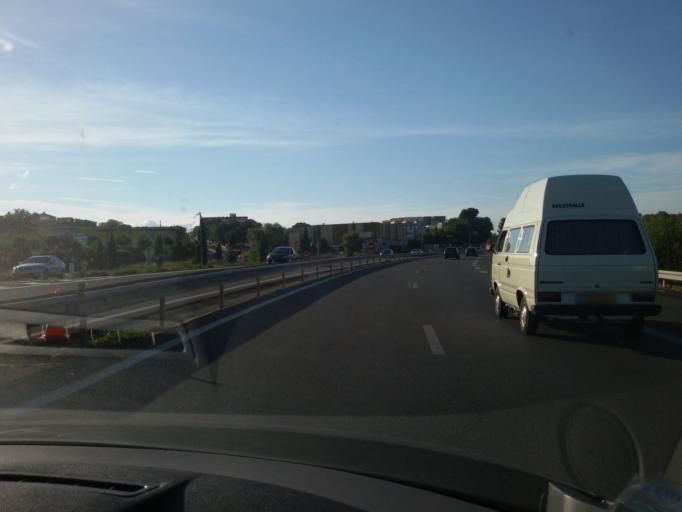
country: FR
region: Languedoc-Roussillon
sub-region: Departement de l'Herault
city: Juvignac
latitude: 43.6190
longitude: 3.7926
